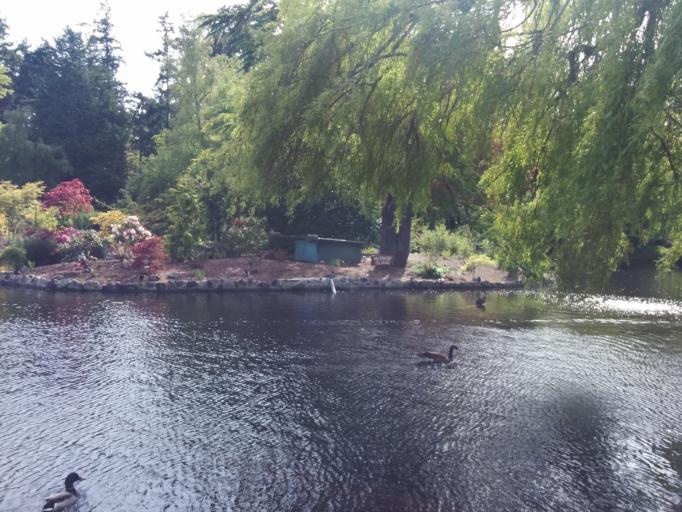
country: CA
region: British Columbia
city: Victoria
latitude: 48.4152
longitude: -123.3639
